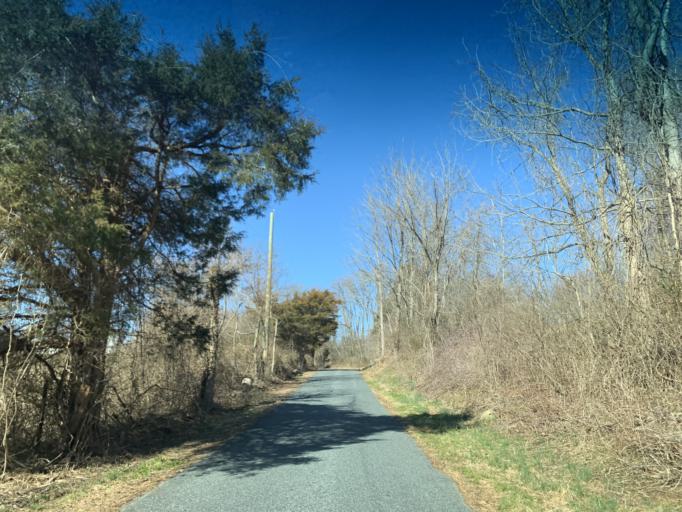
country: US
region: Maryland
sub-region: Harford County
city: Aberdeen
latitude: 39.6226
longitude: -76.2338
